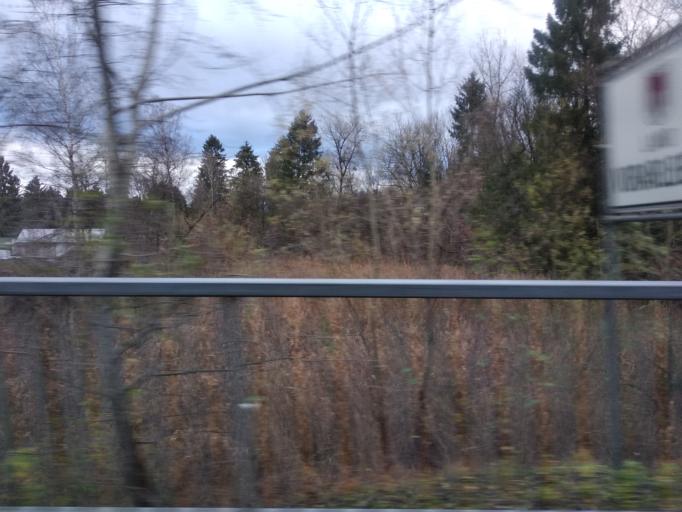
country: AT
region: Vorarlberg
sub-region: Politischer Bezirk Dornbirn
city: Hohenems
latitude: 47.3778
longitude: 9.6709
